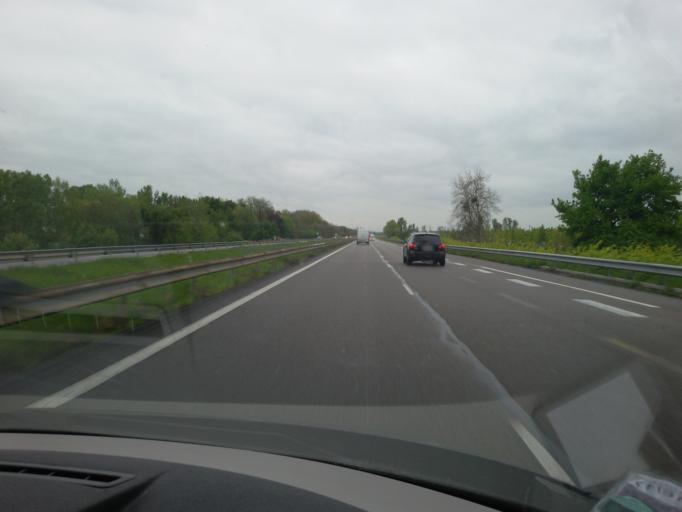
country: FR
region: Rhone-Alpes
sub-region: Departement du Rhone
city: Anse
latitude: 45.9099
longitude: 4.7278
